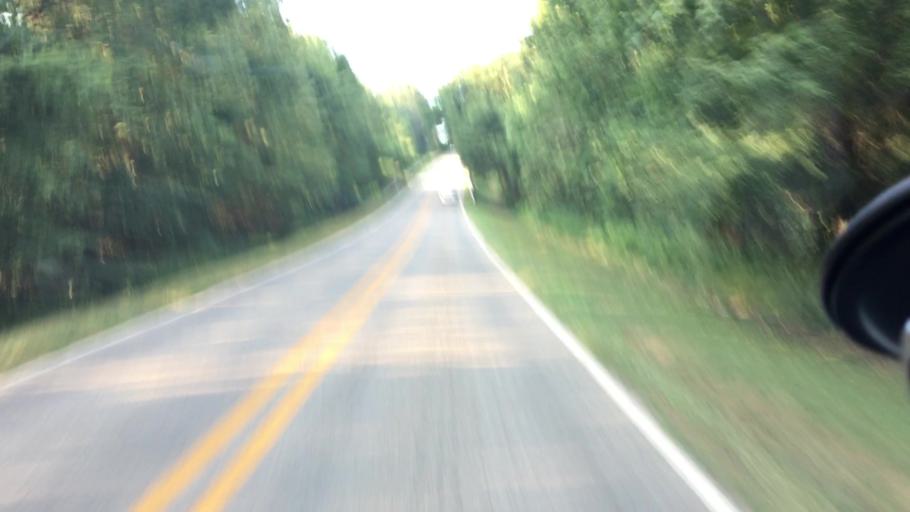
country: US
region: Arkansas
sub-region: Logan County
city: Paris
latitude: 35.3152
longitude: -93.6325
